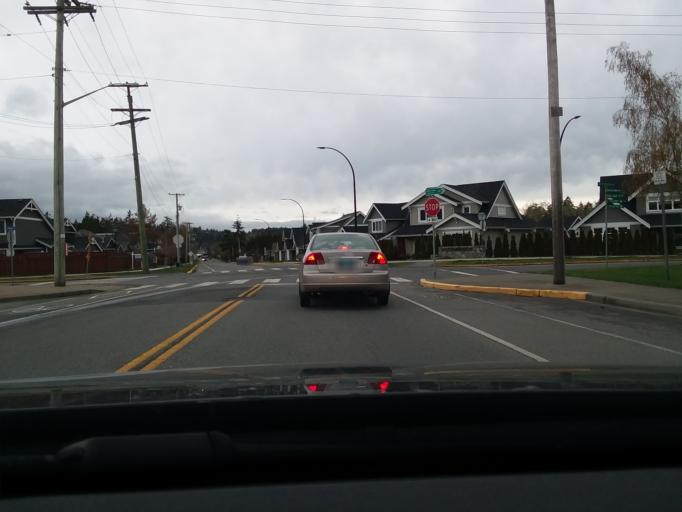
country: CA
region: British Columbia
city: North Saanich
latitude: 48.6659
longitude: -123.4168
